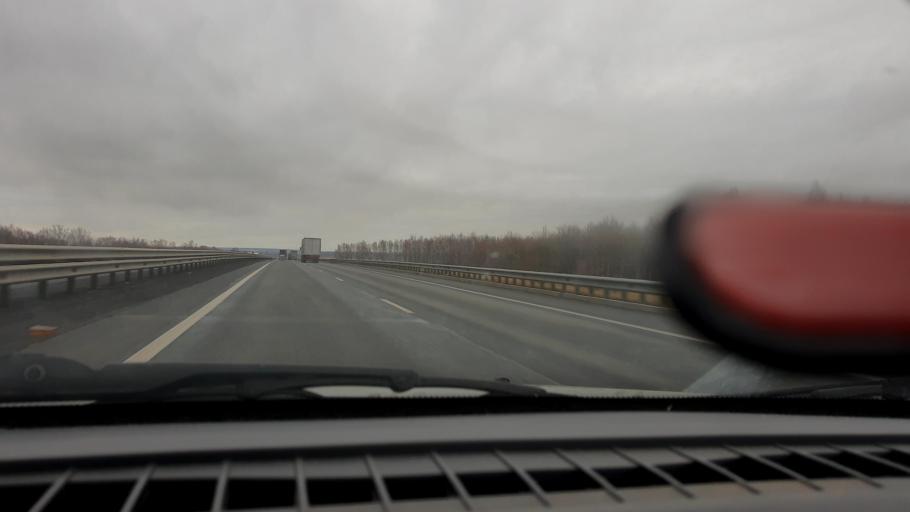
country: RU
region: Nizjnij Novgorod
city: Burevestnik
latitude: 56.1350
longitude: 43.7711
